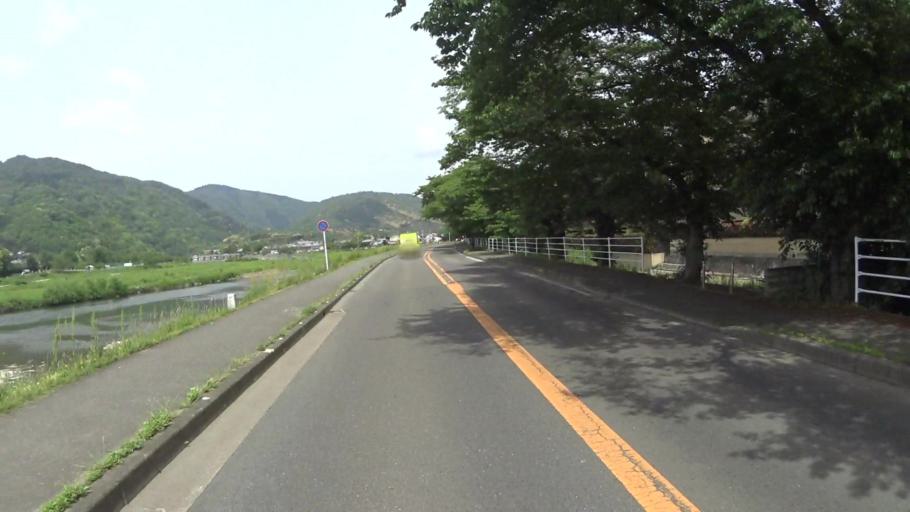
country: JP
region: Kyoto
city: Muko
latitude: 35.0119
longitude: 135.6873
